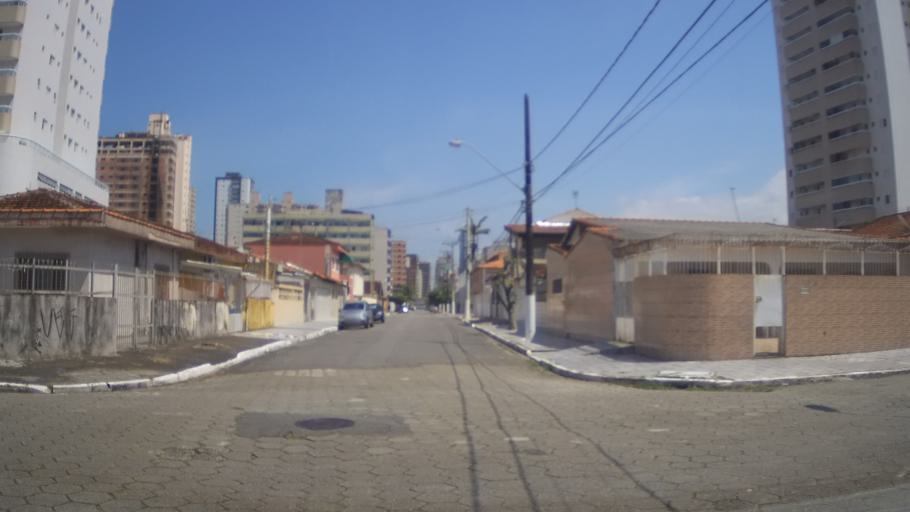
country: BR
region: Sao Paulo
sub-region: Praia Grande
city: Praia Grande
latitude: -24.0174
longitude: -46.4497
